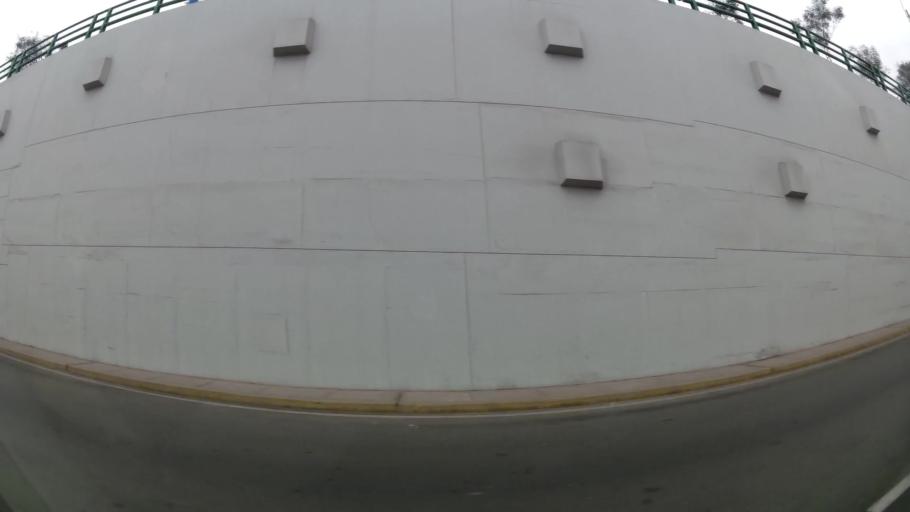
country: PE
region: Lima
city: Ventanilla
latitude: -11.8874
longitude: -77.1260
